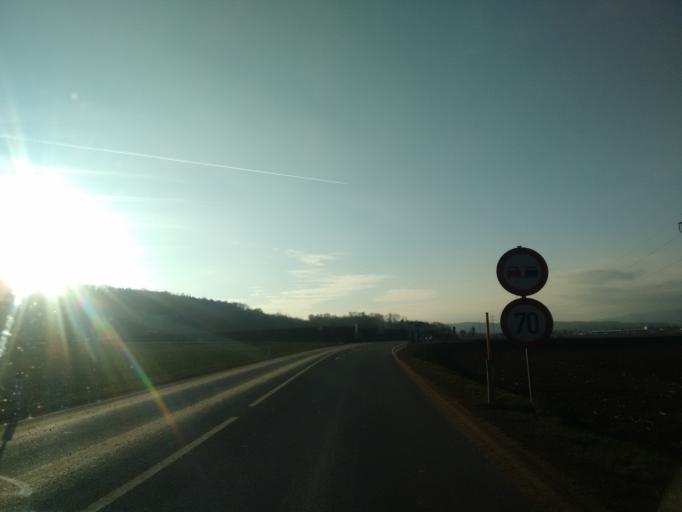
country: AT
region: Lower Austria
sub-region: Politischer Bezirk Melk
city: Klein-Poechlarn
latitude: 48.2012
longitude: 15.2364
